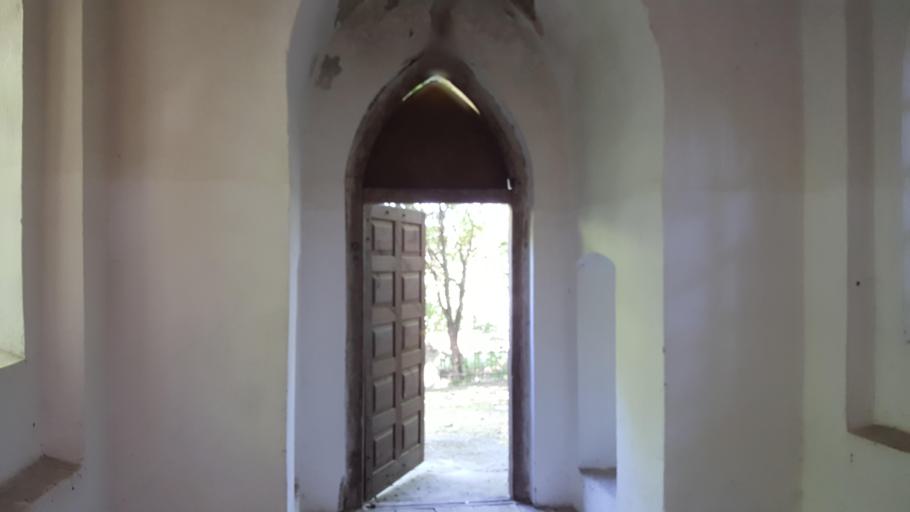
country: PL
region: Lublin Voivodeship
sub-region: Powiat bialski
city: Terespol
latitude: 52.2180
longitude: 23.5101
